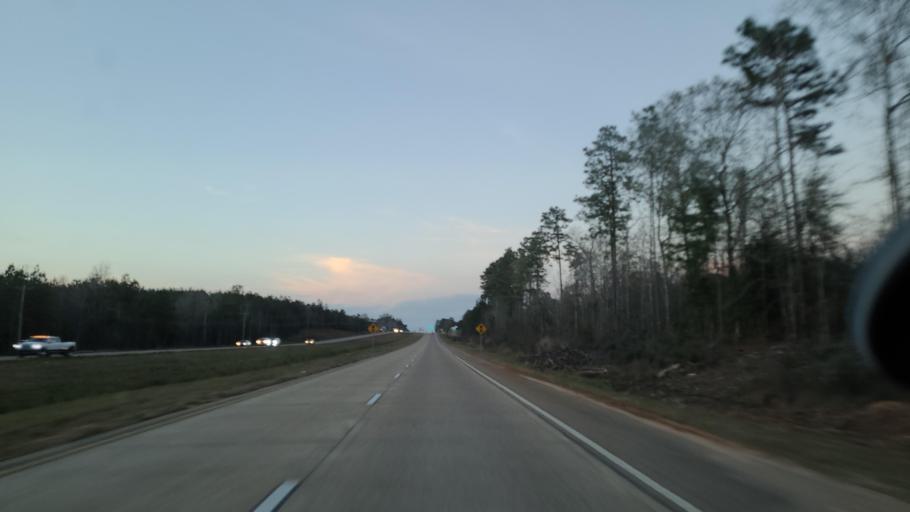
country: US
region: Mississippi
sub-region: Forrest County
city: Hattiesburg
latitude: 31.1797
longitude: -89.2483
